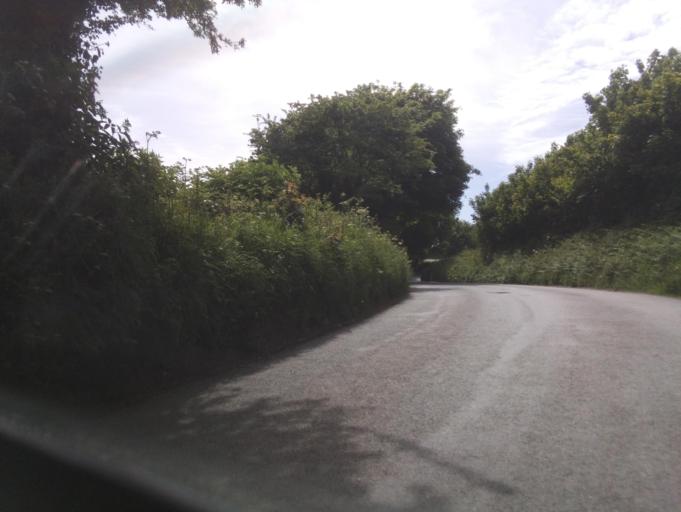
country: GB
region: England
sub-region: Devon
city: Kingsbridge
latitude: 50.3614
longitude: -3.7410
